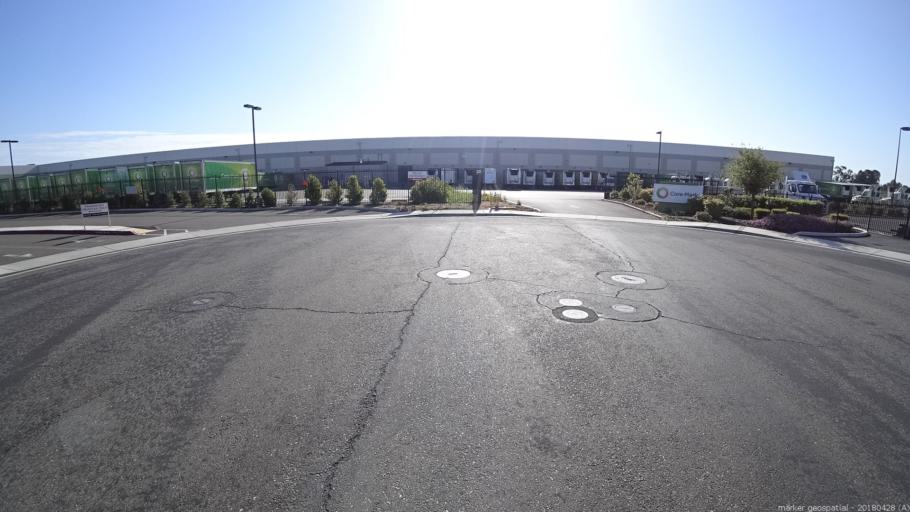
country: US
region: California
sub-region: Yolo County
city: West Sacramento
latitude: 38.5493
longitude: -121.5612
